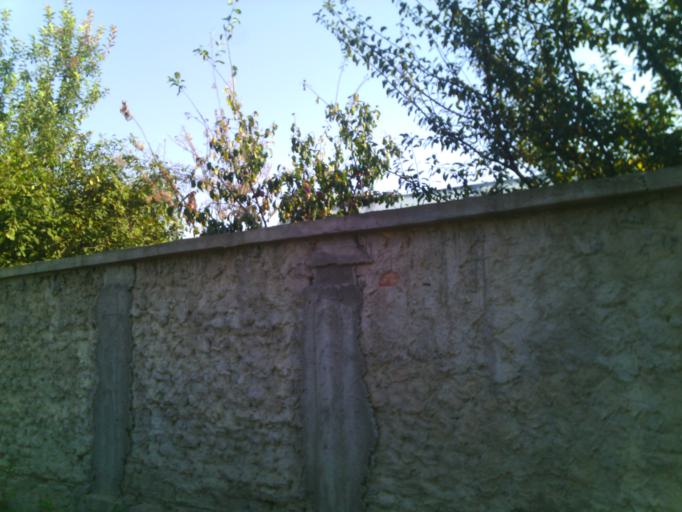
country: RO
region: Giurgiu
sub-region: Comuna Valea Dragului
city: Valea Dragului
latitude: 44.2062
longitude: 26.2758
